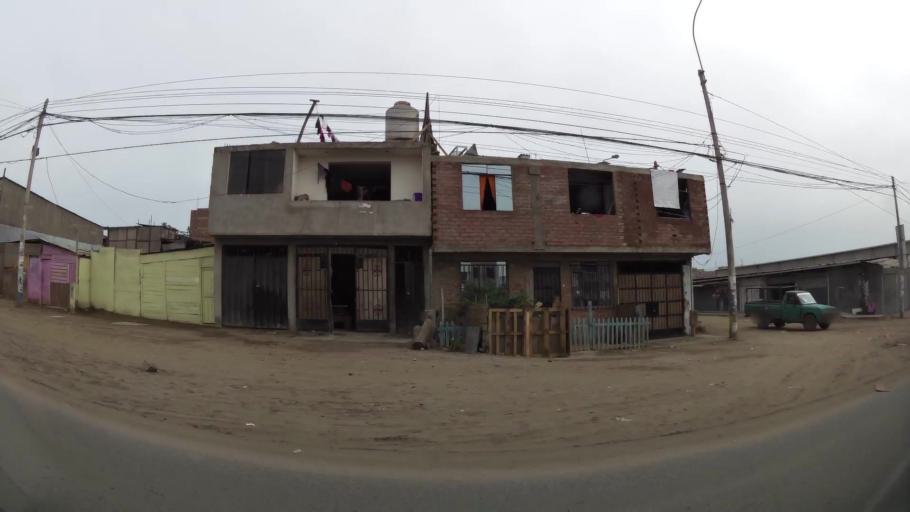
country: PE
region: Lima
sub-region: Lima
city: Surco
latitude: -12.2361
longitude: -76.9399
